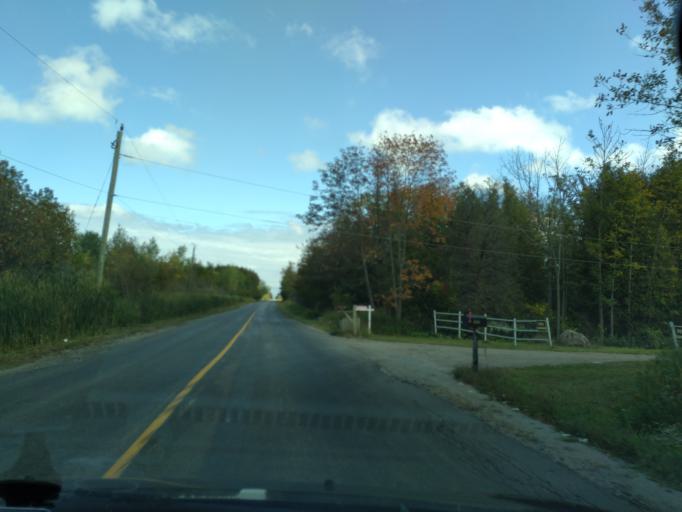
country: CA
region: Ontario
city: Innisfil
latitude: 44.2803
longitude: -79.5897
